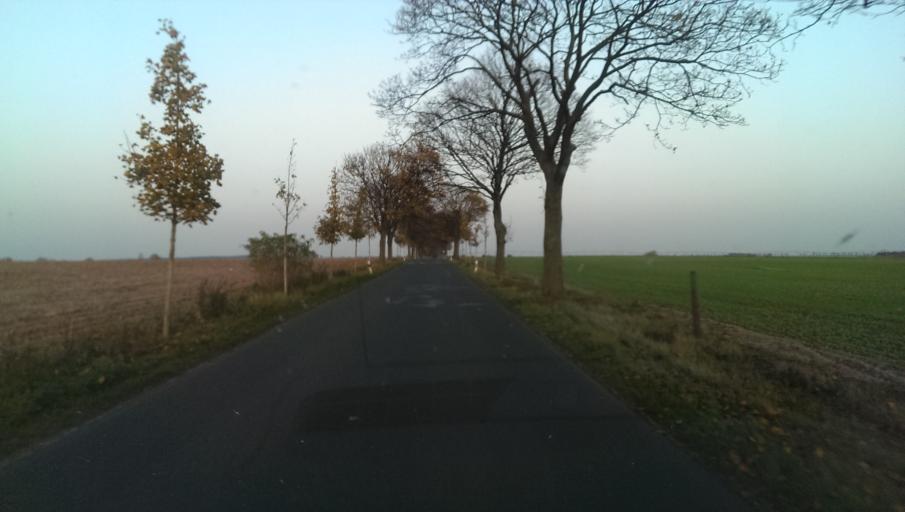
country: DE
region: Brandenburg
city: Juterbog
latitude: 51.9427
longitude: 13.0690
